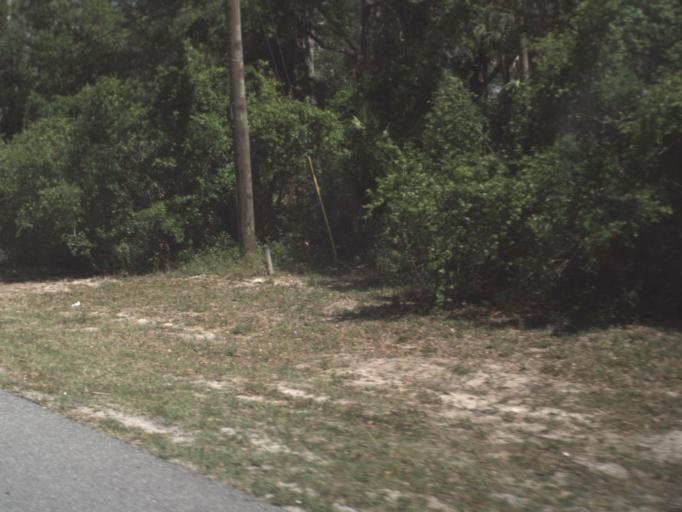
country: US
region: Florida
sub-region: Flagler County
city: Palm Coast
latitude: 29.6108
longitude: -81.2010
